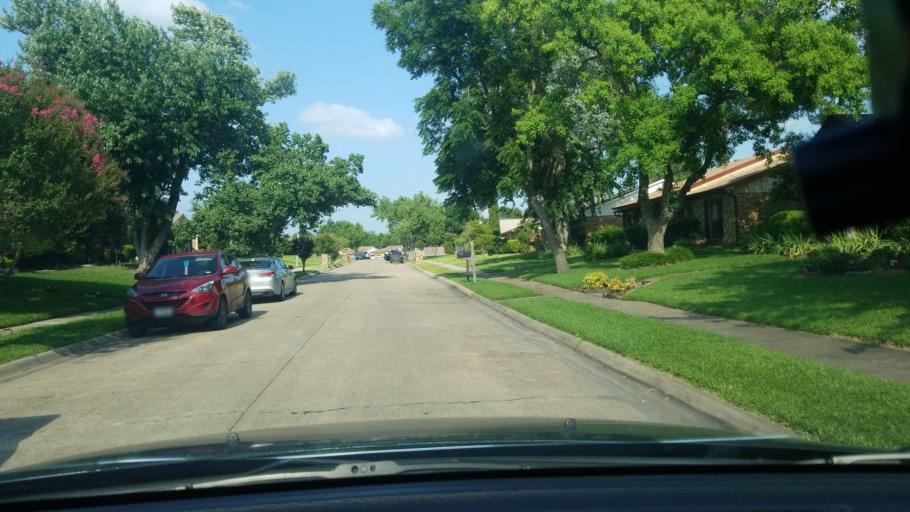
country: US
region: Texas
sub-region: Dallas County
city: Sunnyvale
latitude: 32.8174
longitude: -96.6057
